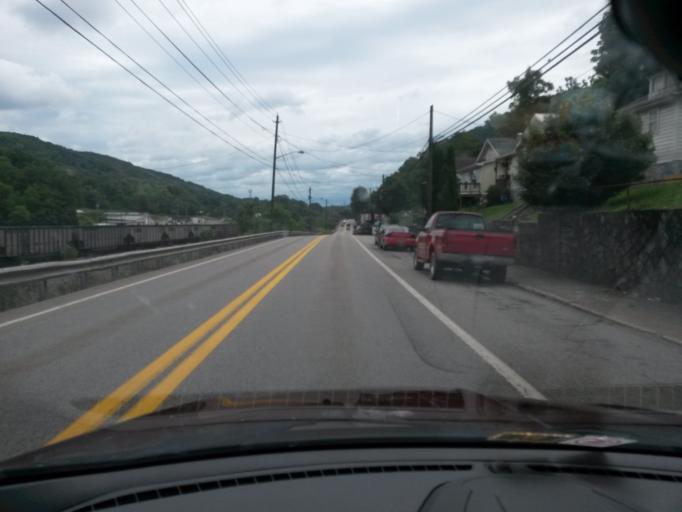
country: US
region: West Virginia
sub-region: Mercer County
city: Bluefield
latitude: 37.2770
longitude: -81.1977
